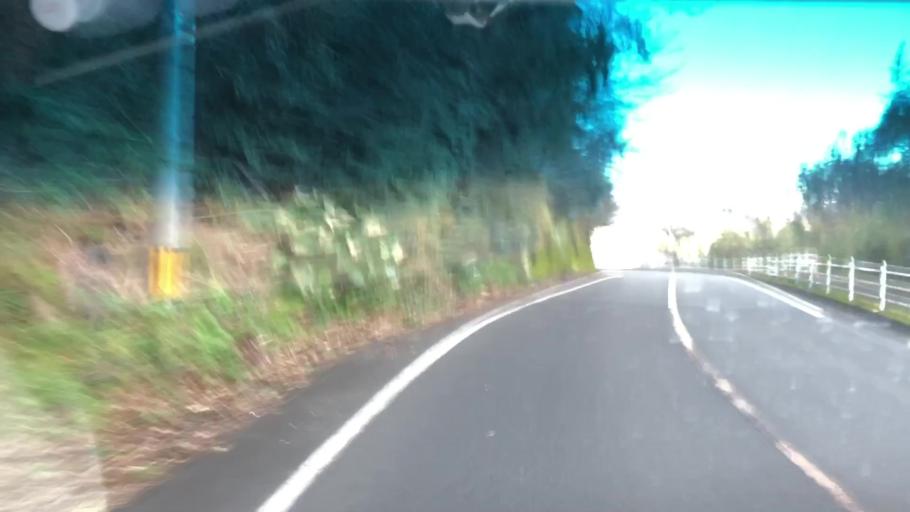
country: JP
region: Kagoshima
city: Satsumasendai
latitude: 31.8162
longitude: 130.2895
